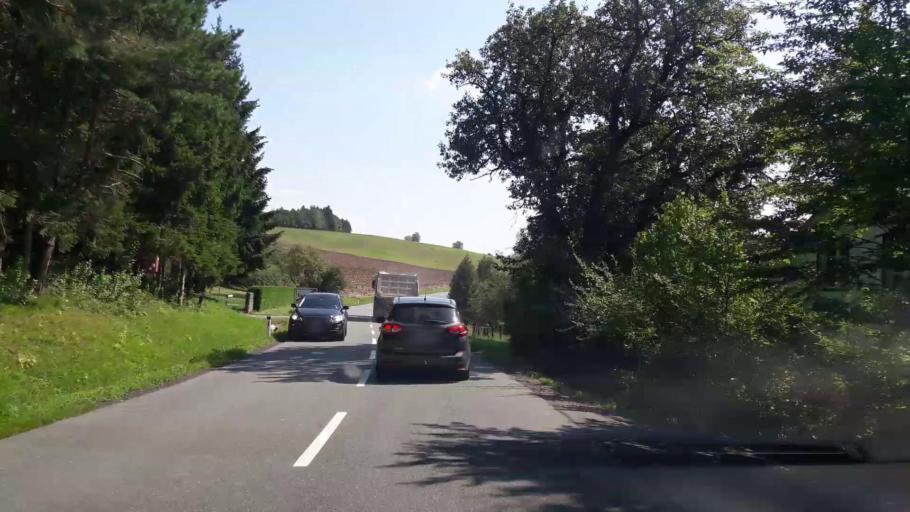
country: AT
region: Styria
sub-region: Politischer Bezirk Hartberg-Fuerstenfeld
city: Stubenberg
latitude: 47.2271
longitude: 15.8111
